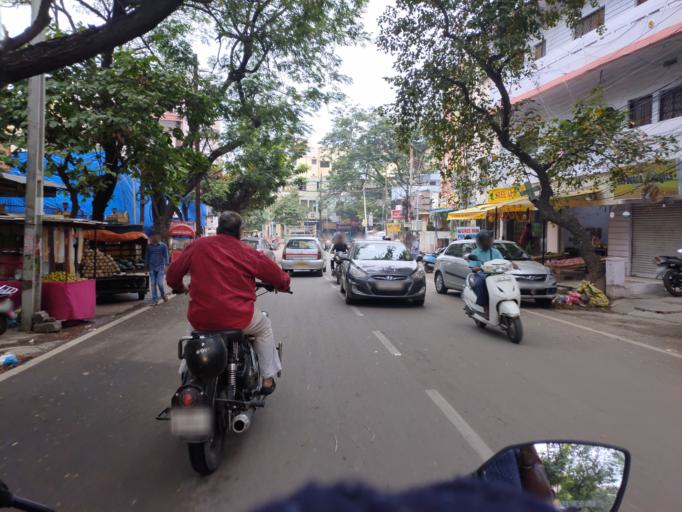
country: IN
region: Telangana
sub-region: Rangareddi
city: Kukatpalli
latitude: 17.4464
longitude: 78.4471
